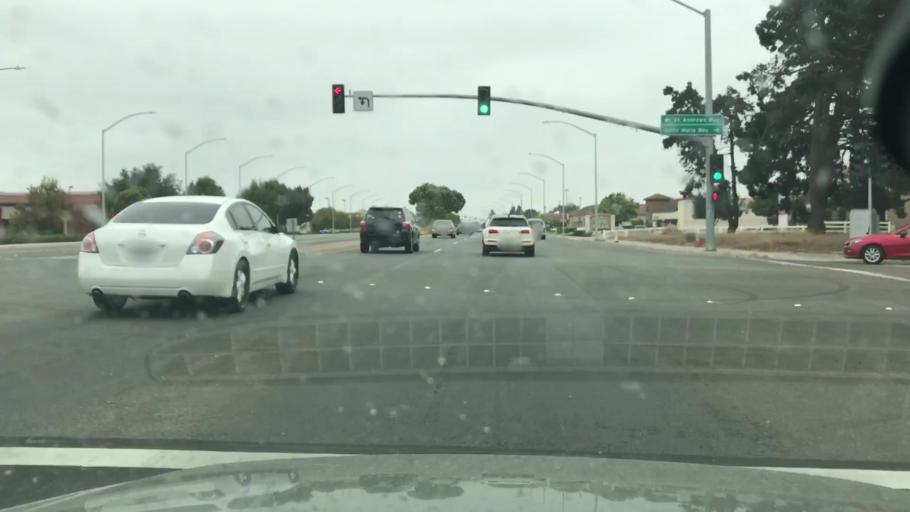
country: US
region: California
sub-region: Santa Barbara County
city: Santa Maria
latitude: 34.9129
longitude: -120.4358
